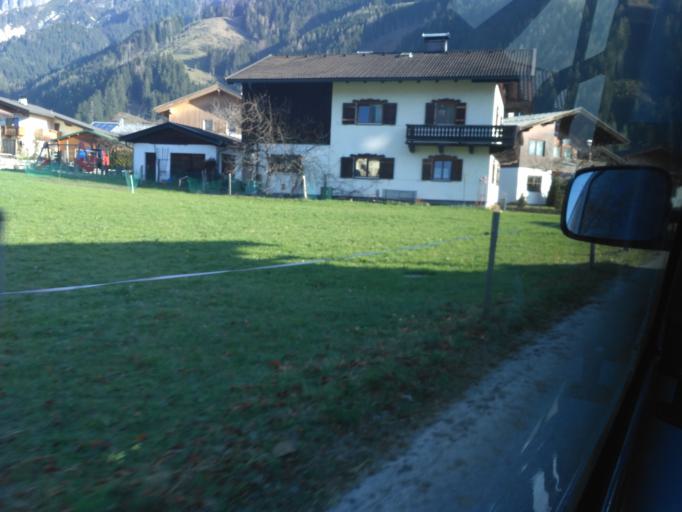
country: AT
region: Salzburg
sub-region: Politischer Bezirk Zell am See
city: Leogang
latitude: 47.4435
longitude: 12.7700
